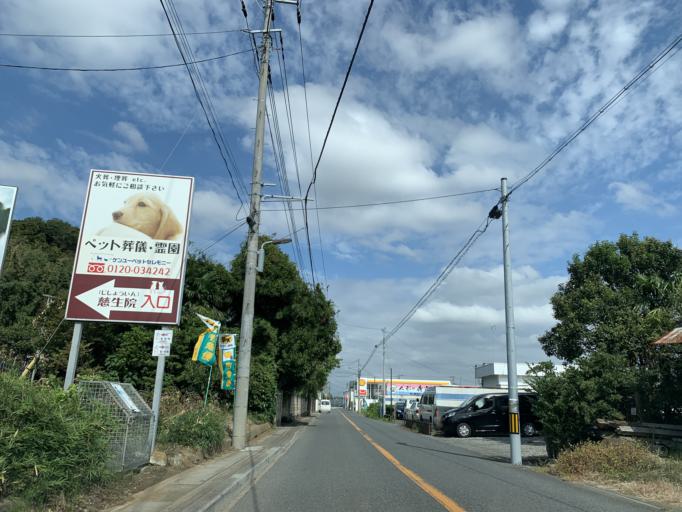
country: JP
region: Chiba
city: Matsudo
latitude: 35.7498
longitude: 139.9178
